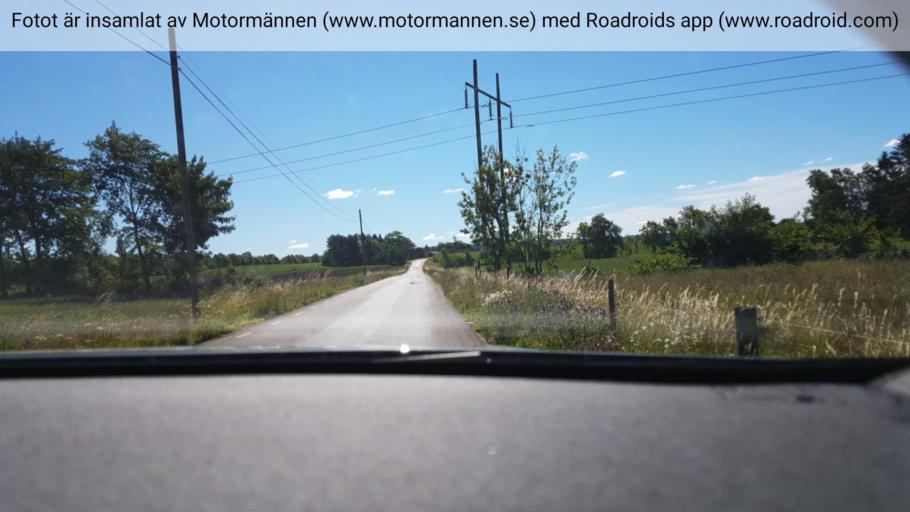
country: SE
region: Vaestra Goetaland
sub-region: Falkopings Kommun
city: Akarp
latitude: 58.2600
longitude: 13.6563
